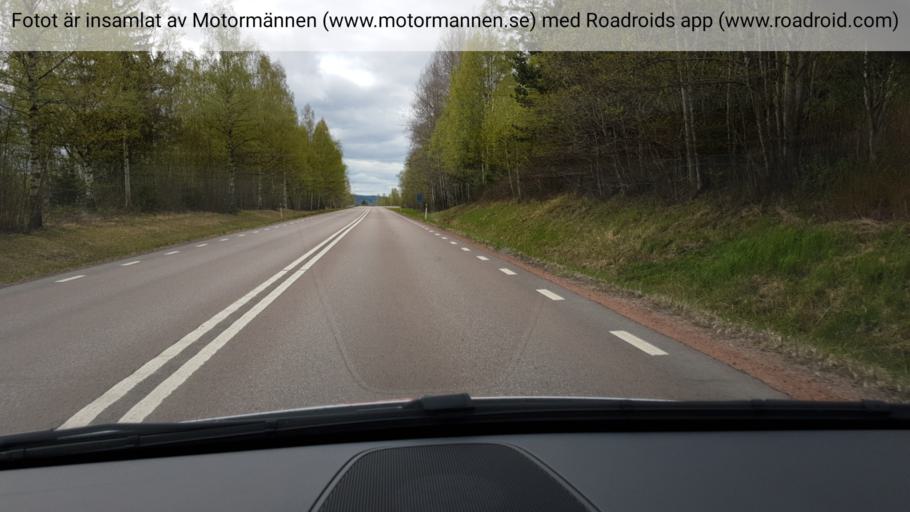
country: SE
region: Jaemtland
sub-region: Ragunda Kommun
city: Hammarstrand
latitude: 63.1401
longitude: 16.0191
